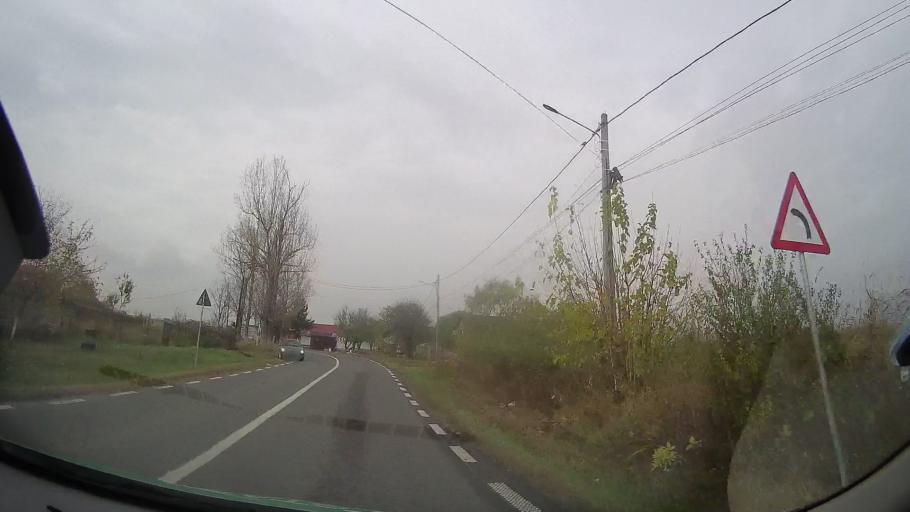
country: RO
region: Ilfov
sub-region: Comuna Gruiu
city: Lipia
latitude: 44.7173
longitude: 26.2489
